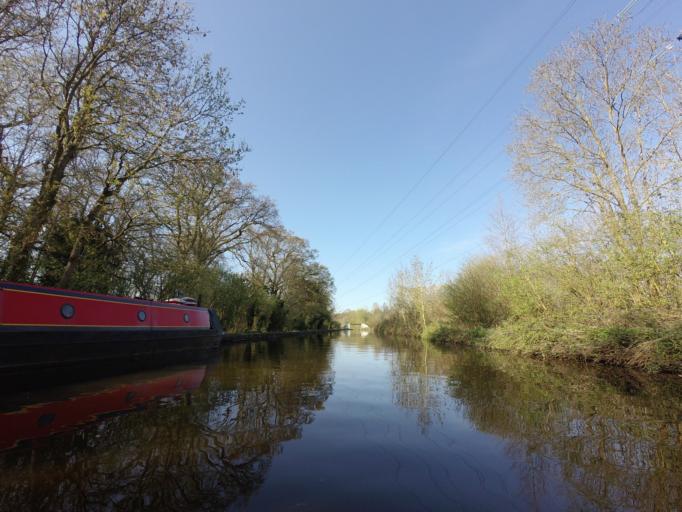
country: GB
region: England
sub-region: Buckinghamshire
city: Denham
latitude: 51.5676
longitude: -0.4823
